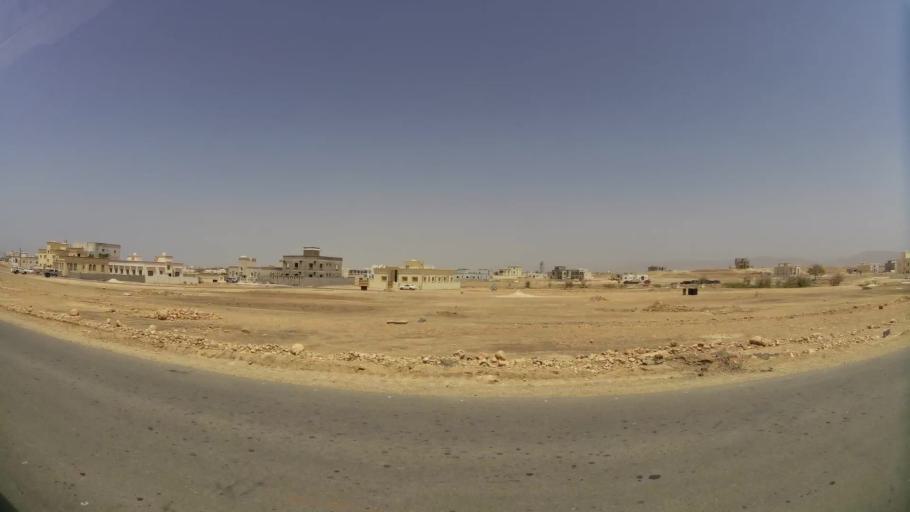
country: OM
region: Zufar
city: Salalah
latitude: 17.0755
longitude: 54.1914
